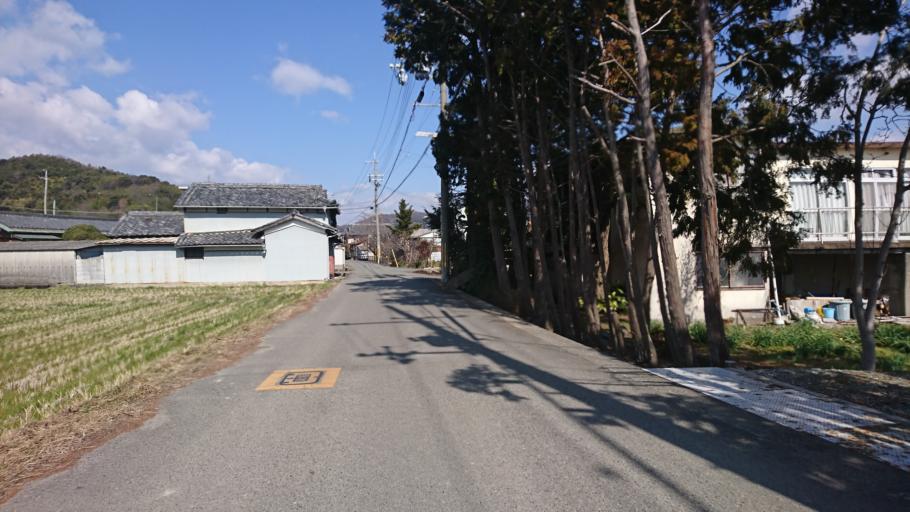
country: JP
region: Hyogo
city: Kakogawacho-honmachi
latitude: 34.8120
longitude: 134.8047
